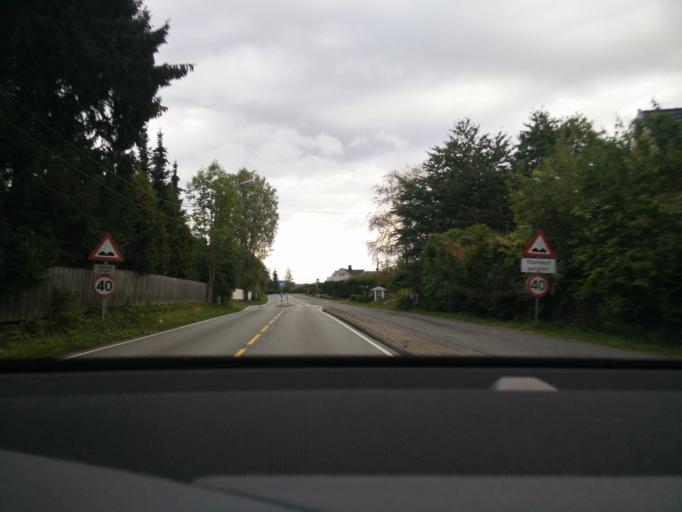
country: NO
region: Akershus
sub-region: Baerum
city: Lysaker
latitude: 59.9313
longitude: 10.6135
